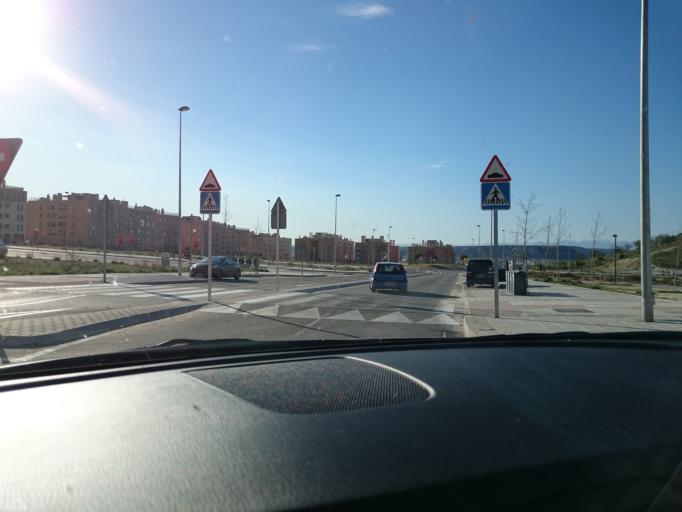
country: ES
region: Madrid
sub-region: Provincia de Madrid
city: Arganda
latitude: 40.2998
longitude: -3.4485
